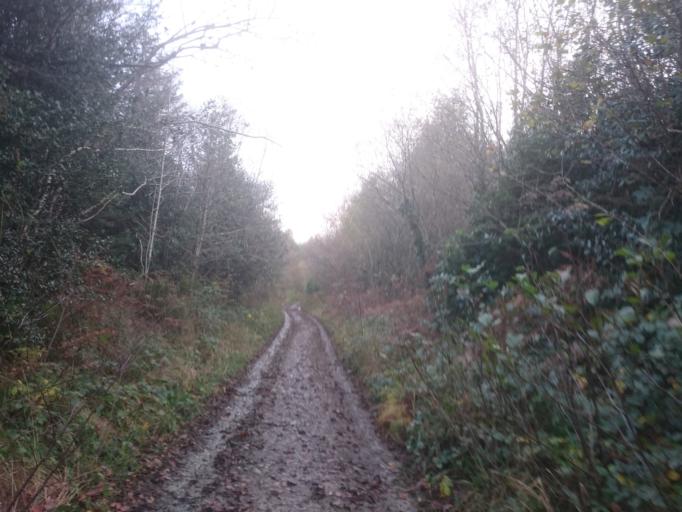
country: IE
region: Leinster
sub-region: Kilkenny
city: Thomastown
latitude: 52.4627
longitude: -7.0548
